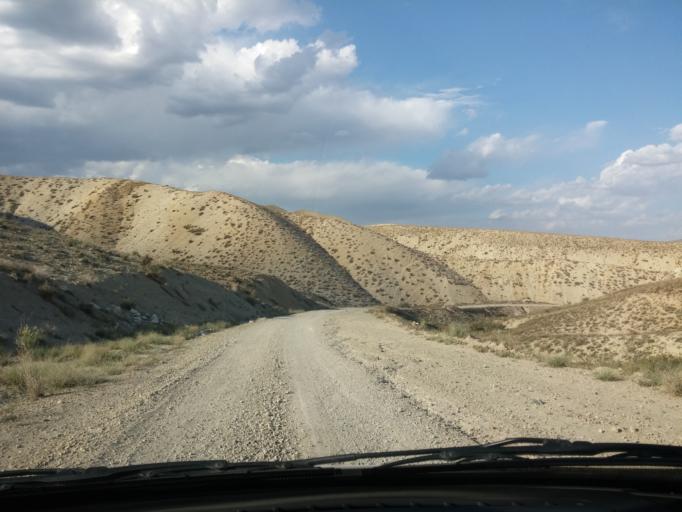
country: IR
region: Tehran
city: Damavand
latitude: 35.5384
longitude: 52.2128
